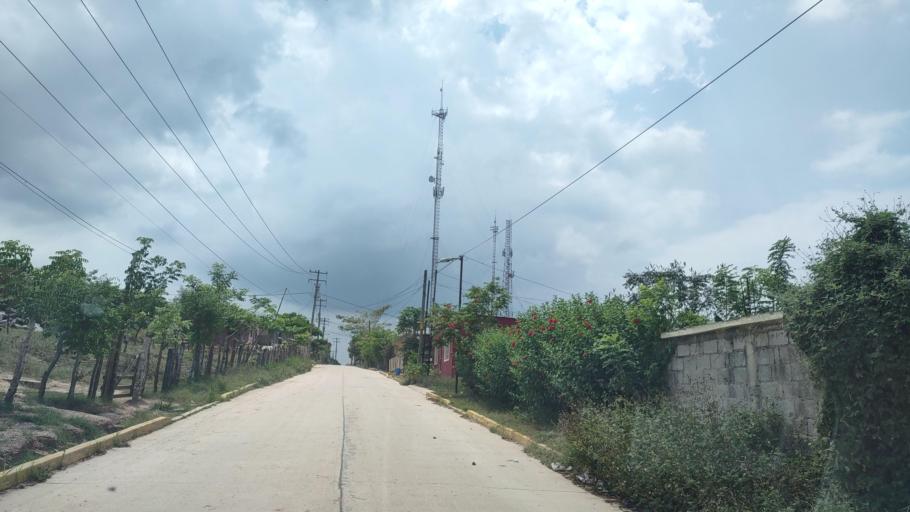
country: MX
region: Veracruz
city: Las Choapas
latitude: 17.9079
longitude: -94.1137
